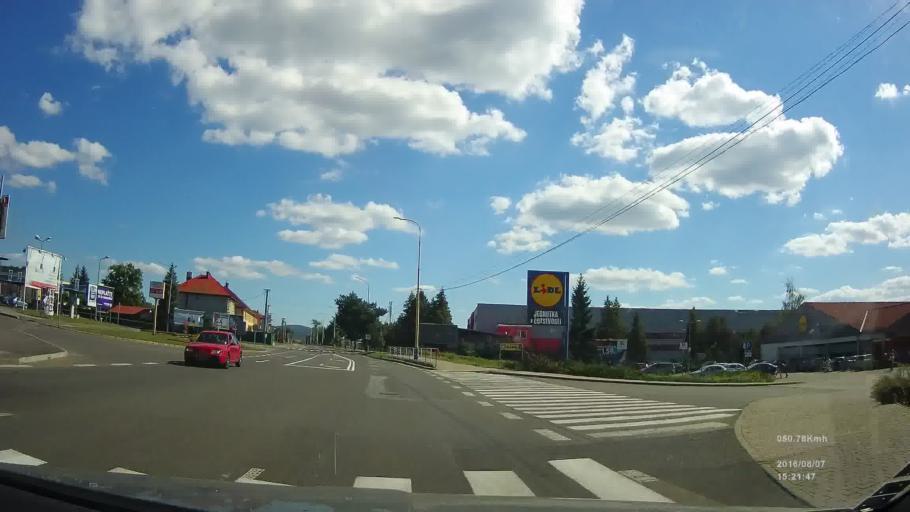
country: SK
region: Presovsky
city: Stropkov
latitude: 49.1978
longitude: 21.6529
